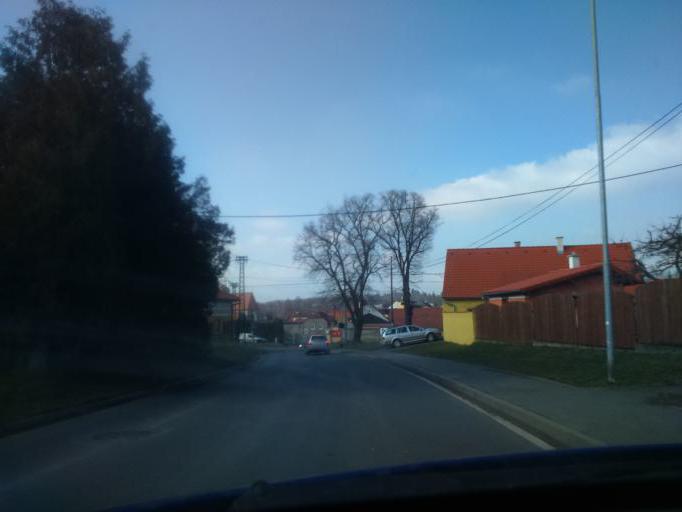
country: CZ
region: Plzensky
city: Horsovsky Tyn
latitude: 49.5247
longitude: 12.9451
